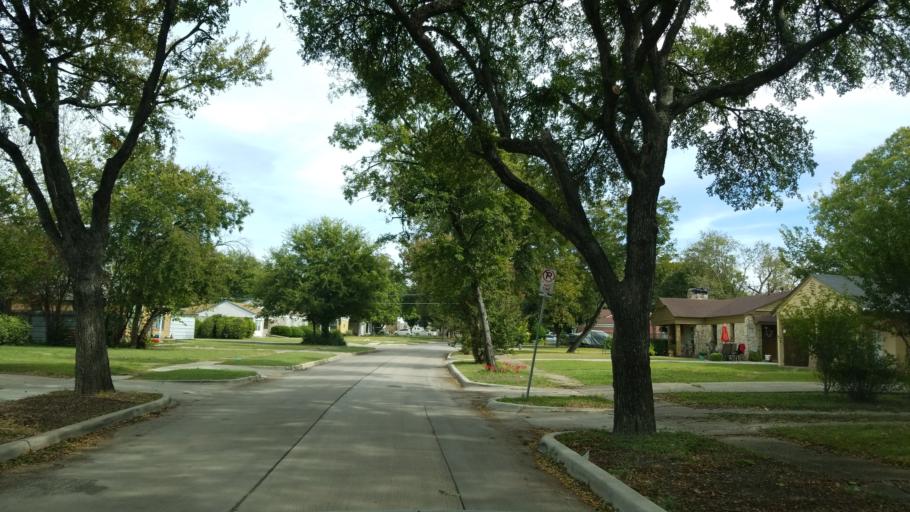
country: US
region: Texas
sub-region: Dallas County
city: Dallas
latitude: 32.7702
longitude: -96.7176
